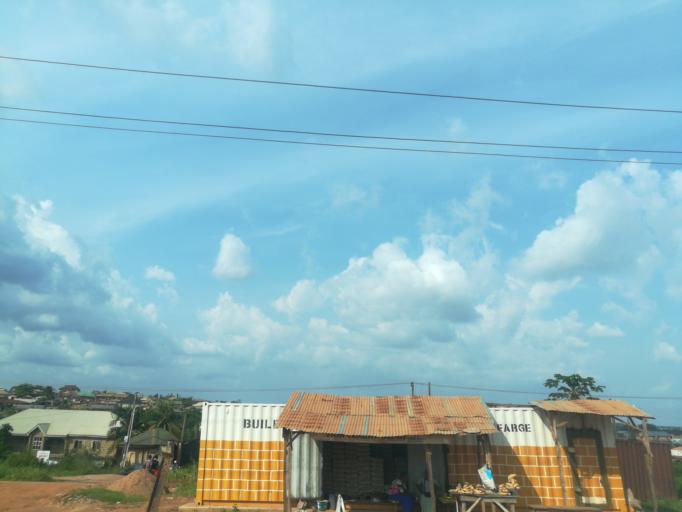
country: NG
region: Oyo
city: Ido
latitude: 7.3989
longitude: 3.8058
